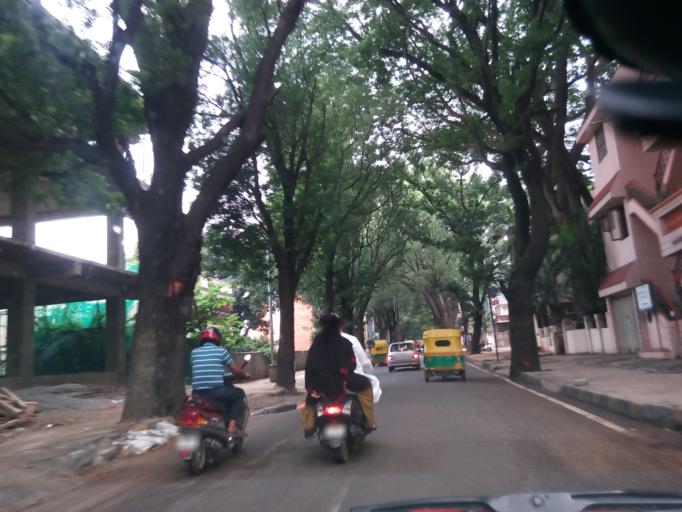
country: IN
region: Karnataka
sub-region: Bangalore Urban
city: Bangalore
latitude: 13.0025
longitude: 77.5692
